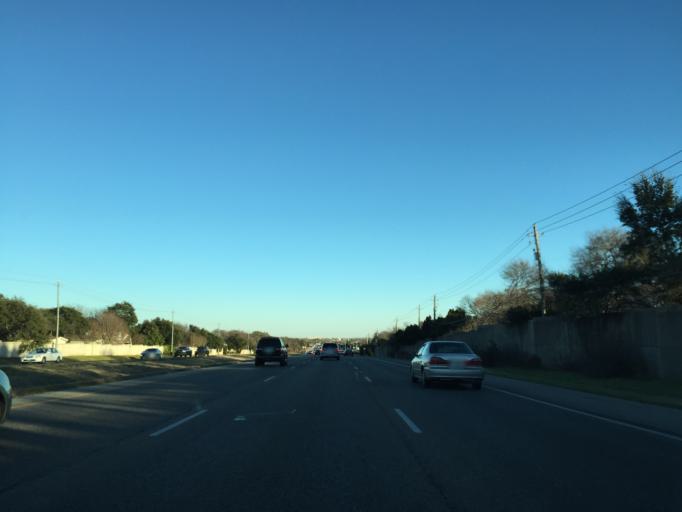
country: US
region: Texas
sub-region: Travis County
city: Wells Branch
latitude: 30.4281
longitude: -97.7206
